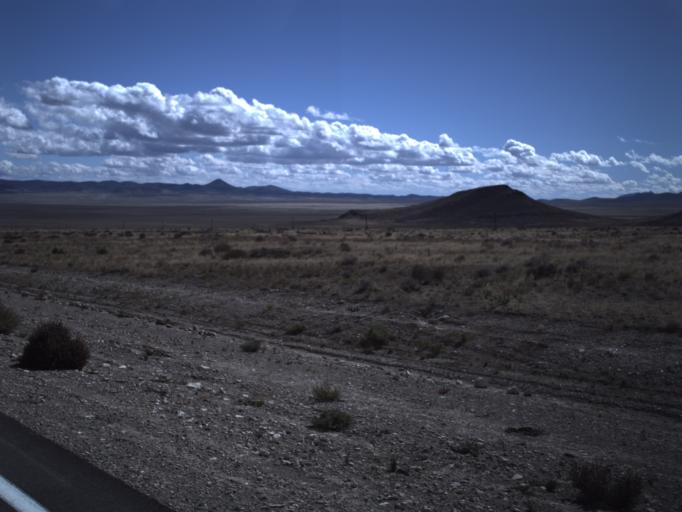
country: US
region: Utah
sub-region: Beaver County
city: Milford
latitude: 38.4929
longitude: -113.4759
